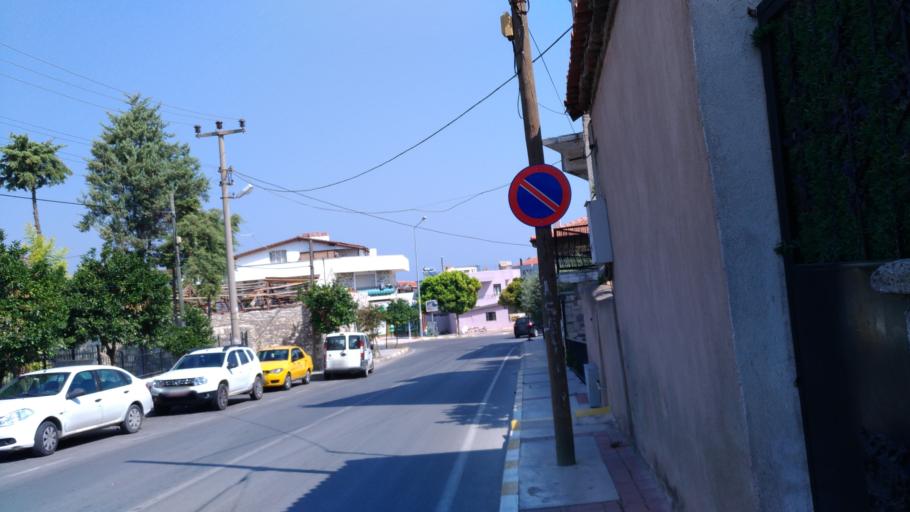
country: TR
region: Izmir
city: Urla
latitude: 38.3229
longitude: 26.7642
